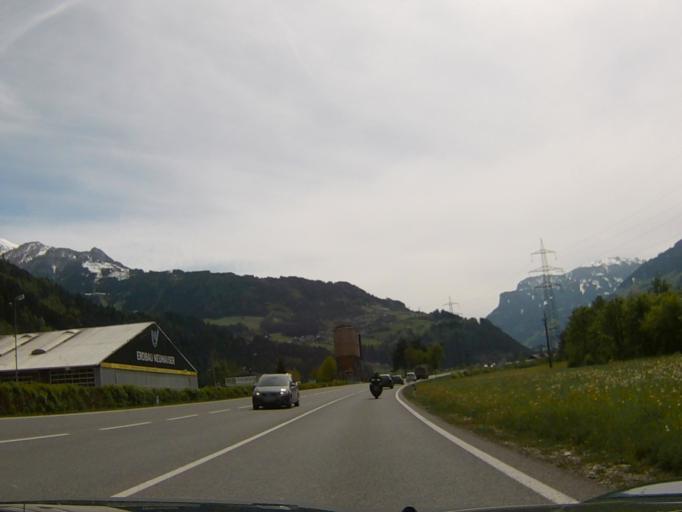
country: AT
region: Tyrol
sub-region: Politischer Bezirk Schwaz
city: Rohrberg
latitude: 47.2438
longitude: 11.9008
